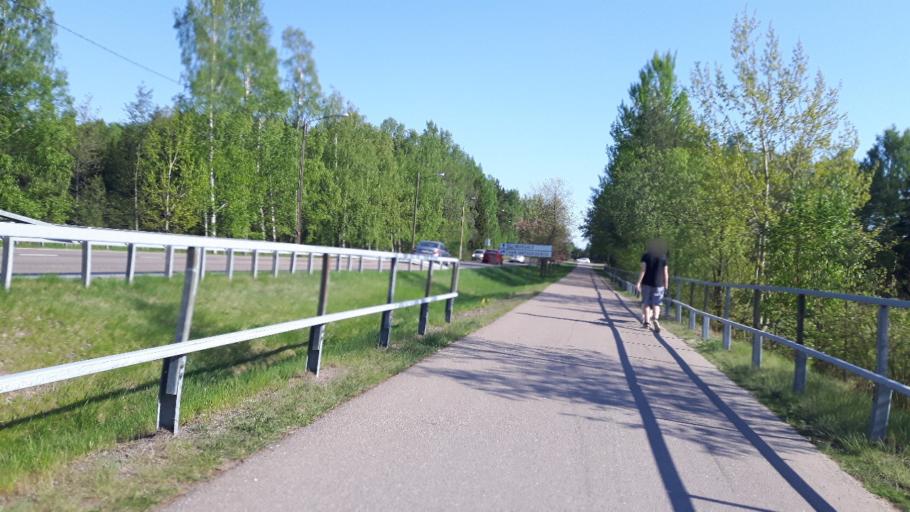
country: FI
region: Kymenlaakso
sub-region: Kotka-Hamina
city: Kotka
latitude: 60.4627
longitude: 26.8832
